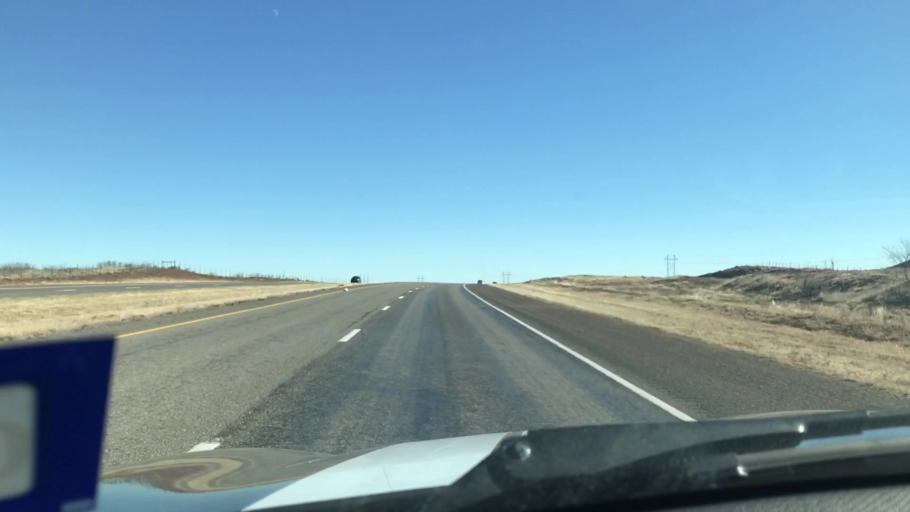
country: US
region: Texas
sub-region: Garza County
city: Post
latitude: 33.1198
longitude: -101.2813
